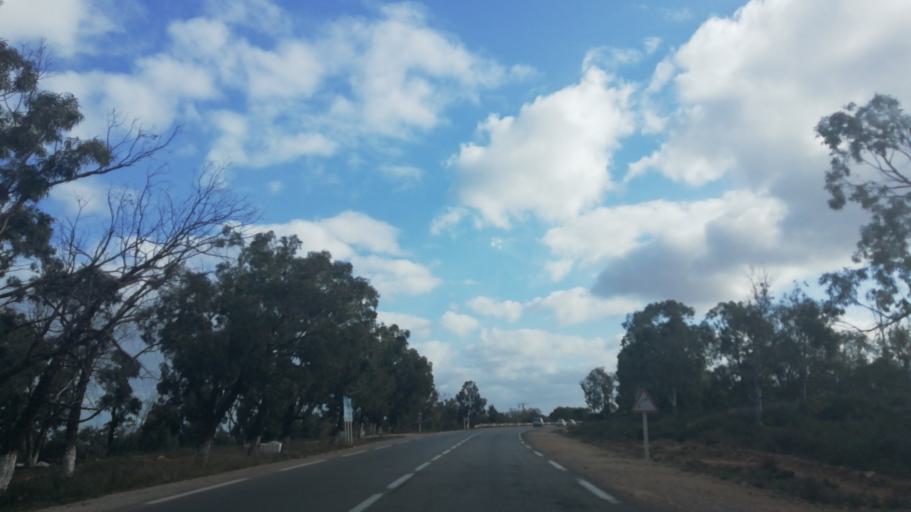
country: DZ
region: Relizane
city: Mazouna
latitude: 36.2383
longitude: 0.5262
